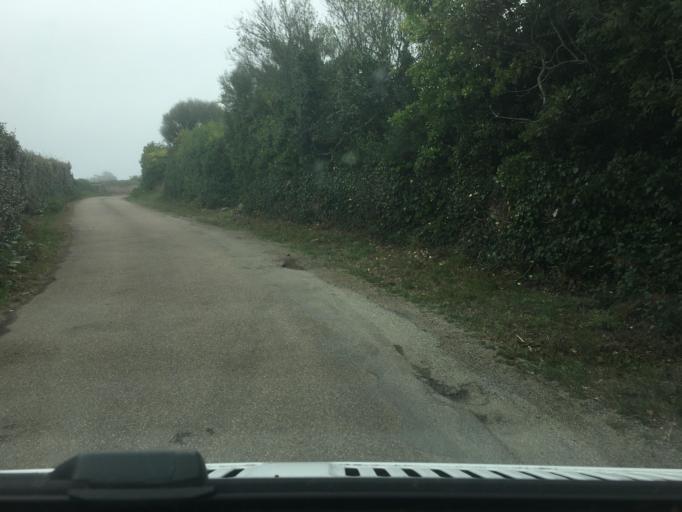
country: FR
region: Brittany
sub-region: Departement du Finistere
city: Plogoff
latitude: 48.0319
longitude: -4.6971
